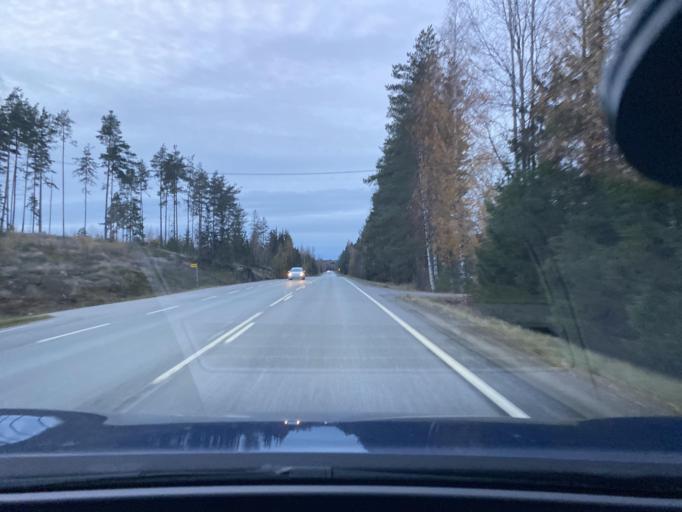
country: FI
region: Uusimaa
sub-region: Helsinki
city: Sammatti
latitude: 60.3866
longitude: 23.8386
